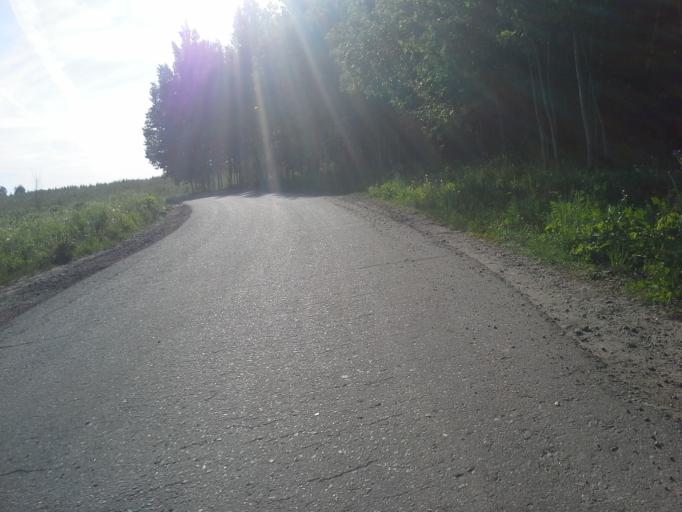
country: RU
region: Moskovskaya
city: Dubrovitsy
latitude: 55.4989
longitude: 37.4386
